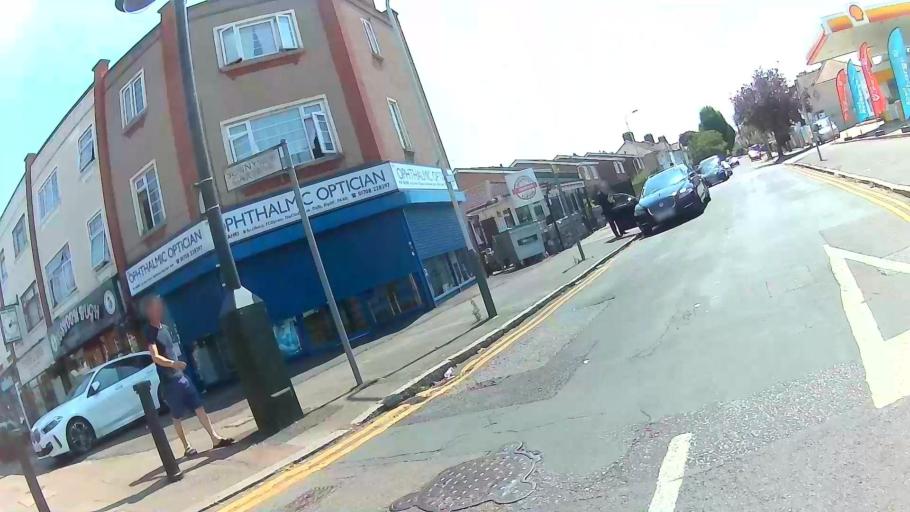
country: GB
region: England
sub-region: Greater London
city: Upminster
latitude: 51.5564
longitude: 0.2511
